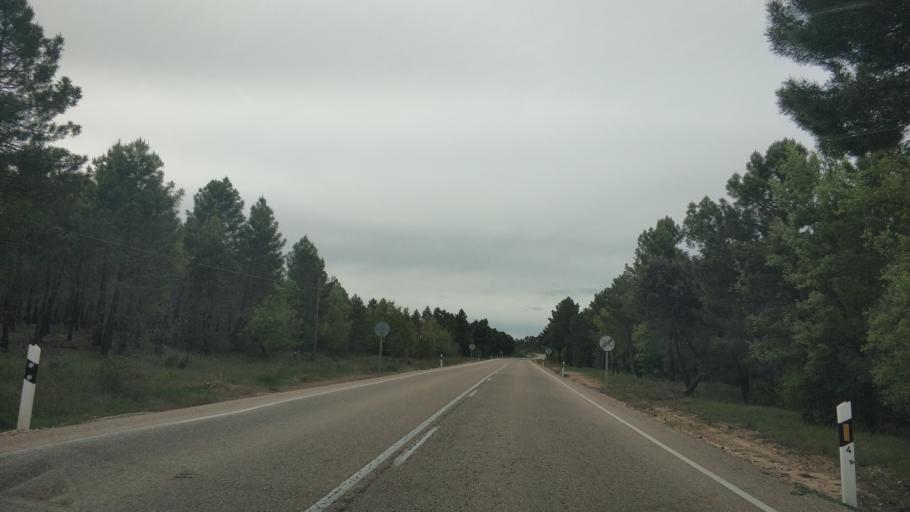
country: ES
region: Castille and Leon
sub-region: Provincia de Soria
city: Bayubas de Abajo
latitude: 41.5135
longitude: -2.9264
